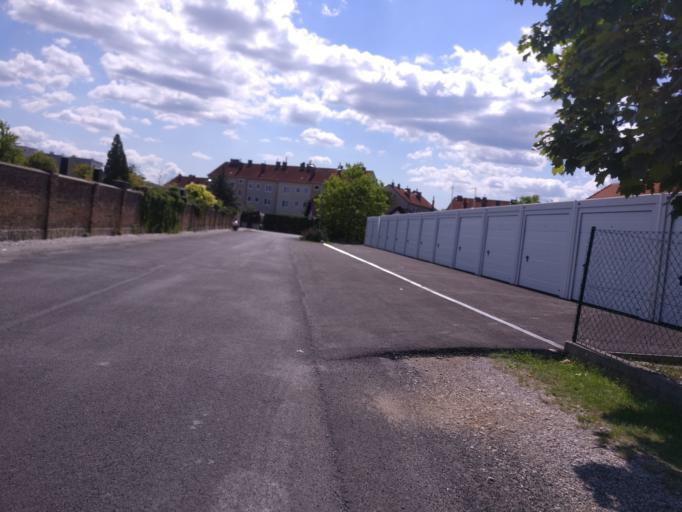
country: AT
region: Lower Austria
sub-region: Politischer Bezirk Neunkirchen
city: Neunkirchen
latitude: 47.7260
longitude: 16.0923
